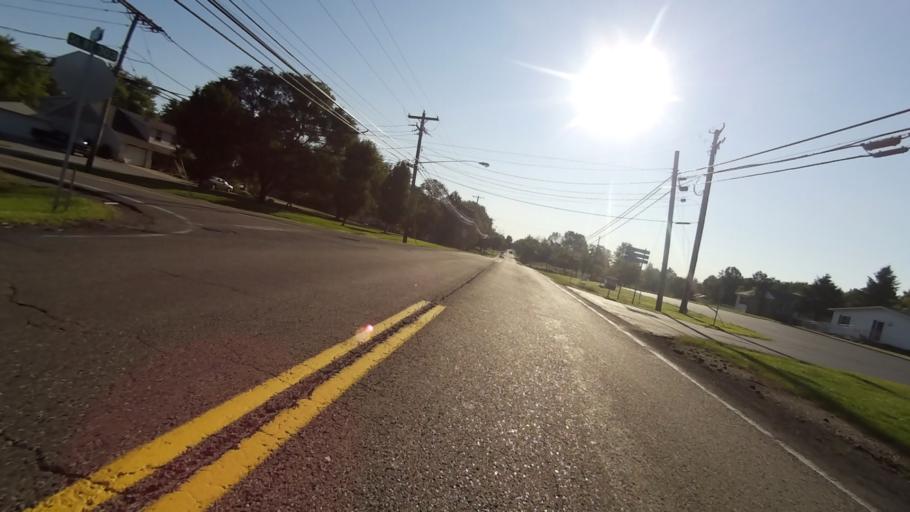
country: US
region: Ohio
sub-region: Portage County
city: Streetsboro
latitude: 41.2390
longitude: -81.3269
